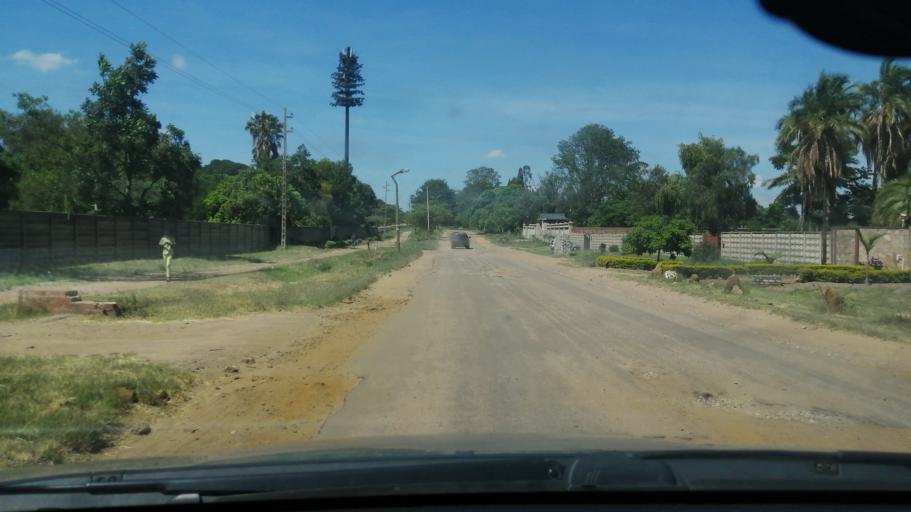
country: ZW
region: Harare
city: Epworth
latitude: -17.8208
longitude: 31.1286
